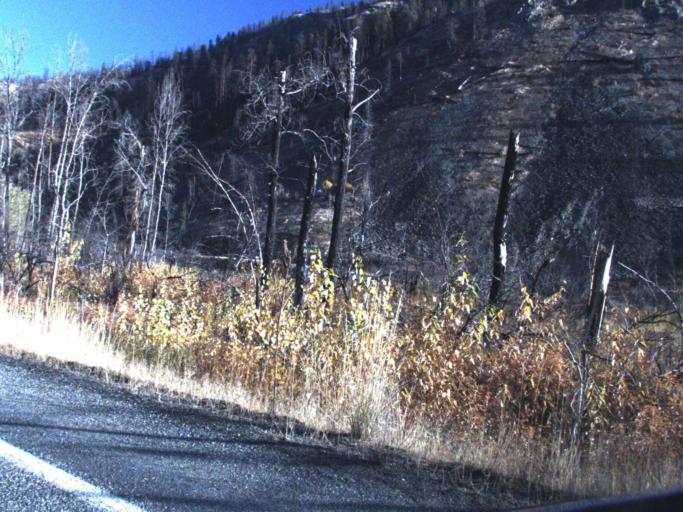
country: US
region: Washington
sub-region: Ferry County
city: Republic
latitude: 48.2641
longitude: -118.6925
